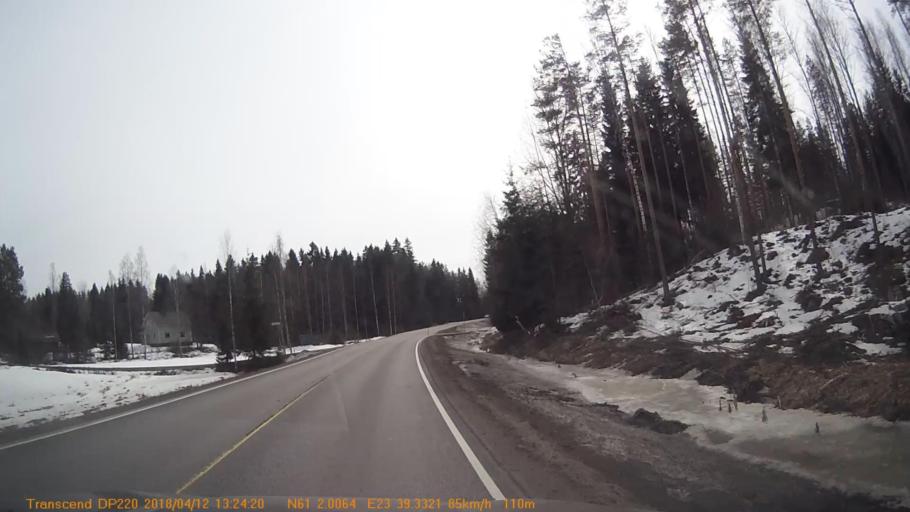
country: FI
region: Pirkanmaa
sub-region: Etelae-Pirkanmaa
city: Kylmaekoski
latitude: 61.0323
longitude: 23.6557
